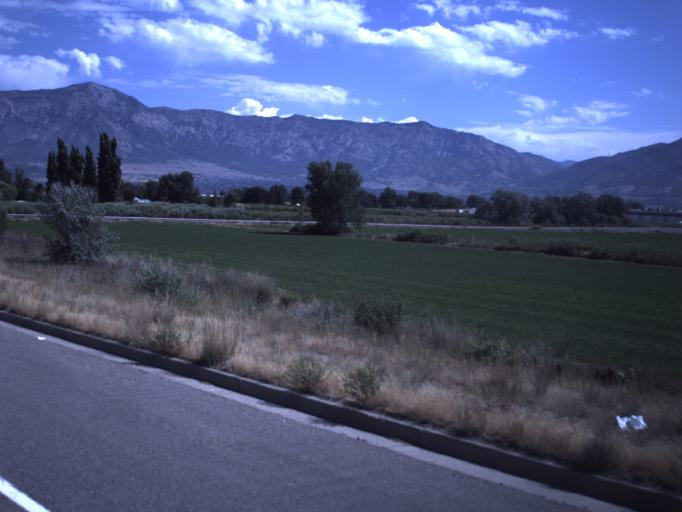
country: US
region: Utah
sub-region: Weber County
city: Marriott-Slaterville
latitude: 41.2467
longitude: -112.0252
